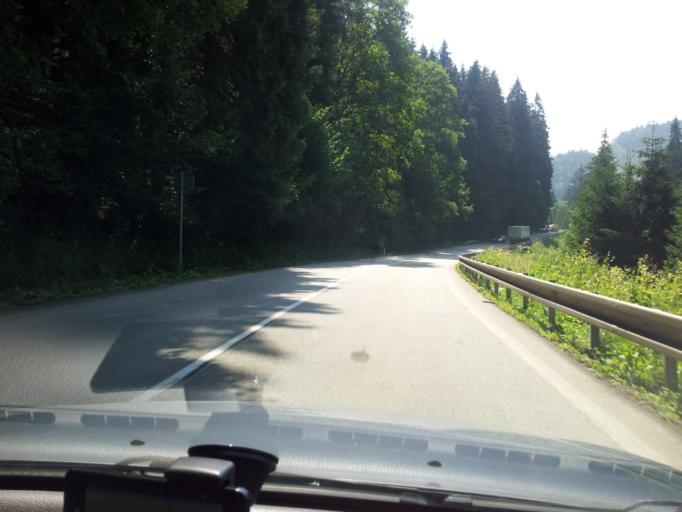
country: SK
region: Zilinsky
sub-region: Okres Dolny Kubin
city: Dolny Kubin
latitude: 49.2742
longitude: 19.3502
